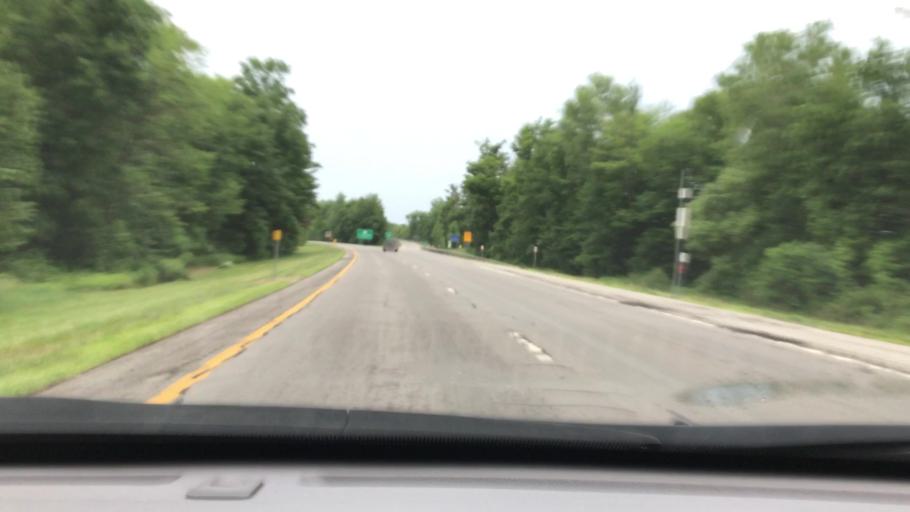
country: US
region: New York
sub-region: Erie County
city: Orchard Park
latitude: 42.7437
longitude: -78.7611
